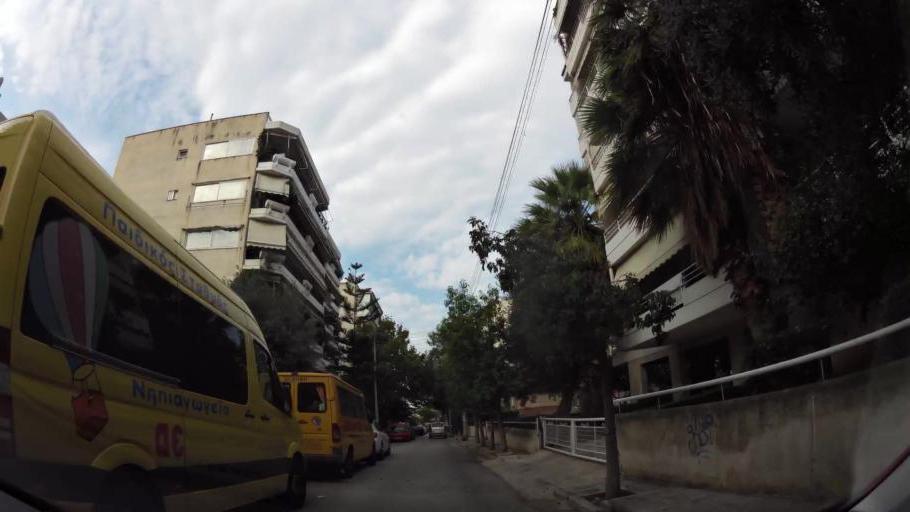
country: GR
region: Attica
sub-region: Nomarchia Athinas
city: Palaio Faliro
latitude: 37.9300
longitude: 23.7085
